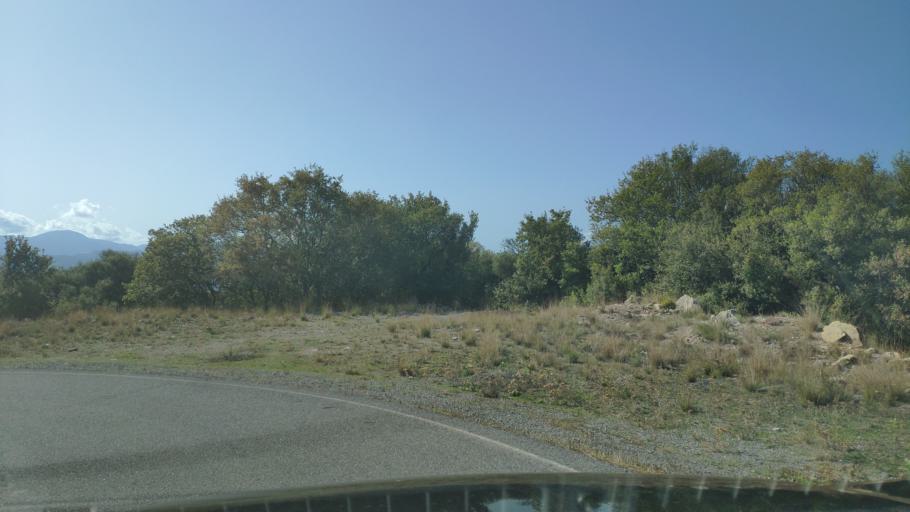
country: GR
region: Peloponnese
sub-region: Nomos Arkadias
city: Dimitsana
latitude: 37.5641
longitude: 21.9996
